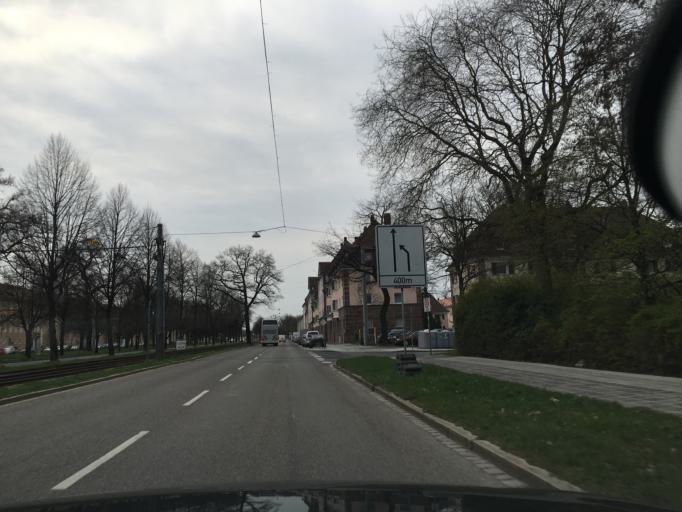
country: DE
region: Bavaria
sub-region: Regierungsbezirk Mittelfranken
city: Nuernberg
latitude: 49.4414
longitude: 11.1078
